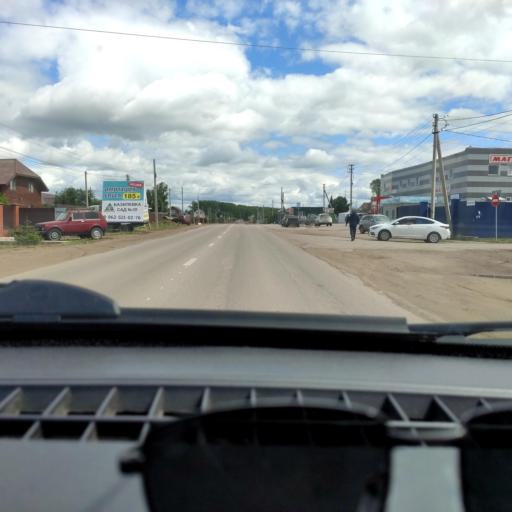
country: RU
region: Bashkortostan
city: Ufa
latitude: 54.6741
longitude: 56.0893
